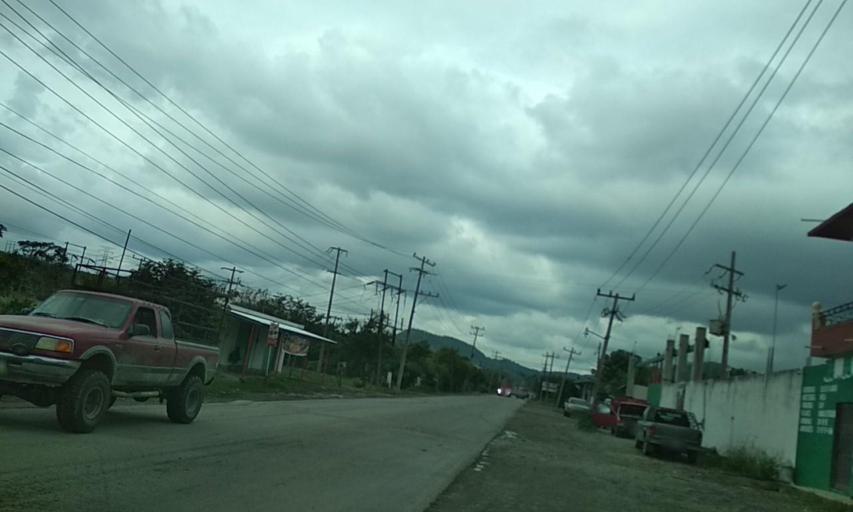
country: MX
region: Veracruz
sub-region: Papantla
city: El Chote
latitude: 20.3962
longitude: -97.3362
